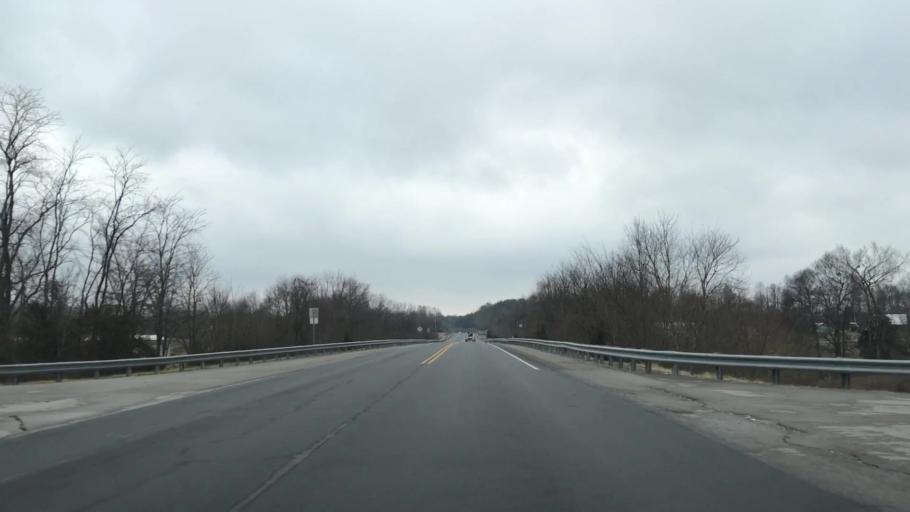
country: US
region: Kentucky
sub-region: Metcalfe County
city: Edmonton
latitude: 36.9568
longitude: -85.4395
